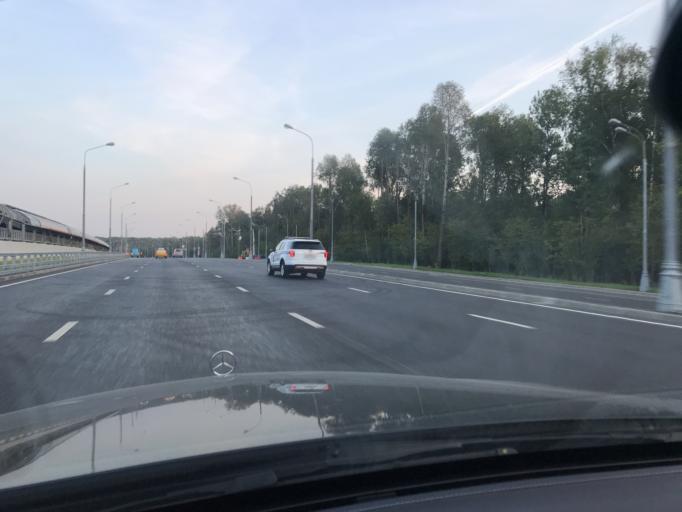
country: RU
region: Moskovskaya
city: Mosrentgen
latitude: 55.5942
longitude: 37.4183
